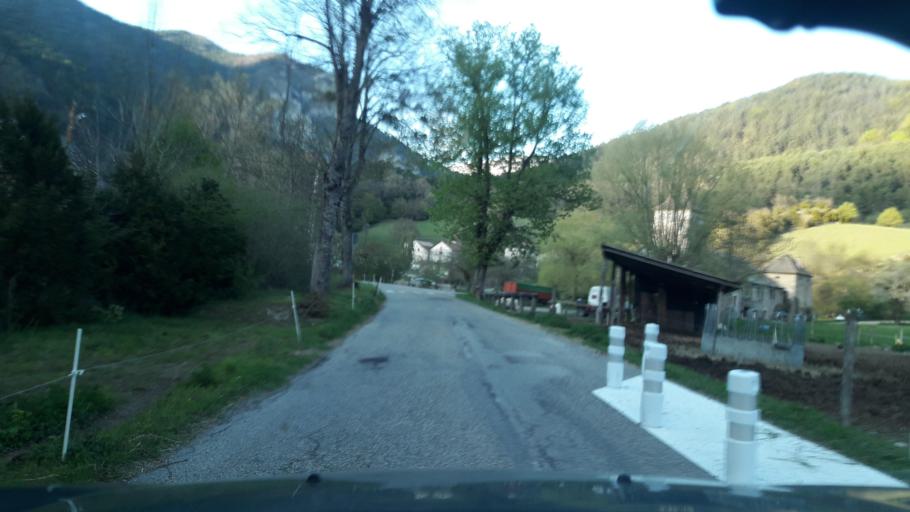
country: FR
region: Rhone-Alpes
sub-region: Departement de l'Isere
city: Mens
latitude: 44.6854
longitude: 5.5954
